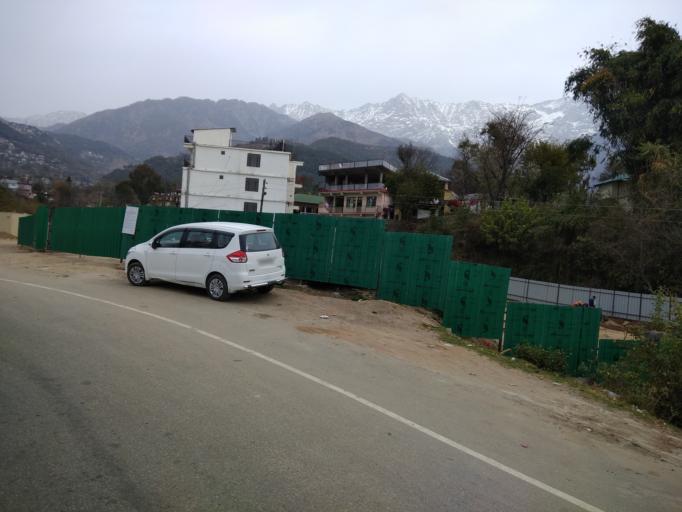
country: IN
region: Himachal Pradesh
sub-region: Kangra
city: Dharmsala
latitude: 32.2053
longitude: 76.3289
